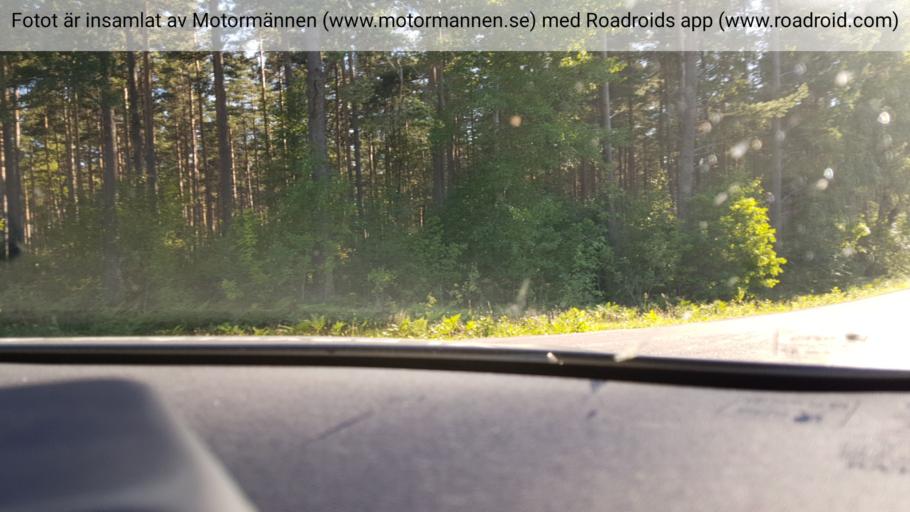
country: SE
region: Vaestra Goetaland
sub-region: Tidaholms Kommun
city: Tidaholm
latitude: 58.1377
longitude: 13.9670
